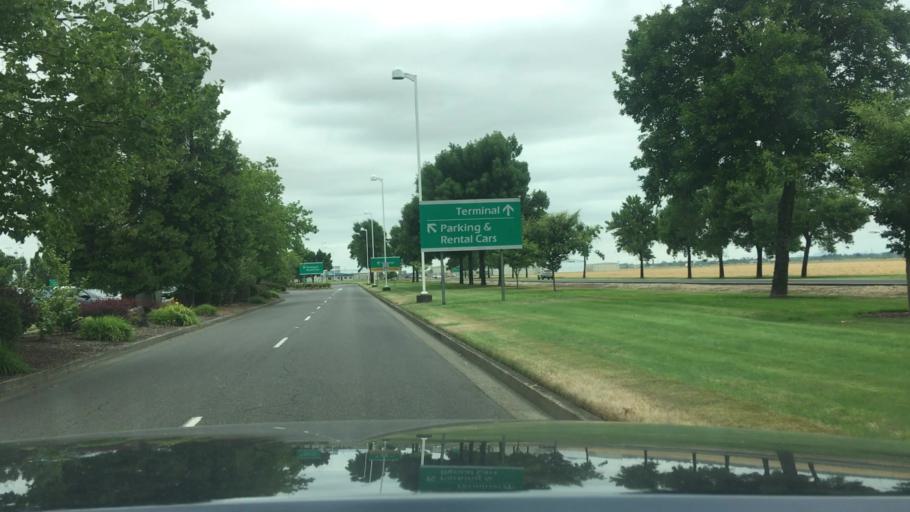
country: US
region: Oregon
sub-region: Lane County
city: Junction City
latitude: 44.1180
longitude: -123.2088
